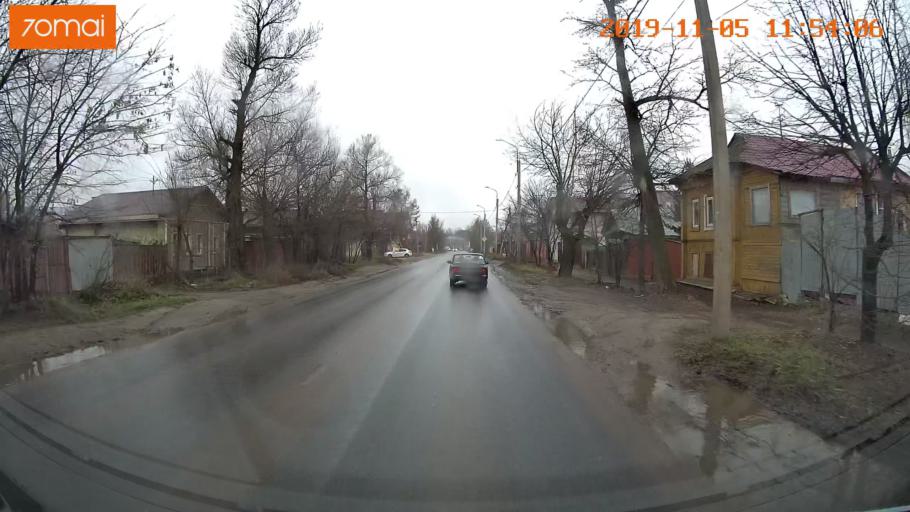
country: RU
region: Ivanovo
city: Bogorodskoye
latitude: 56.9928
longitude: 41.0309
